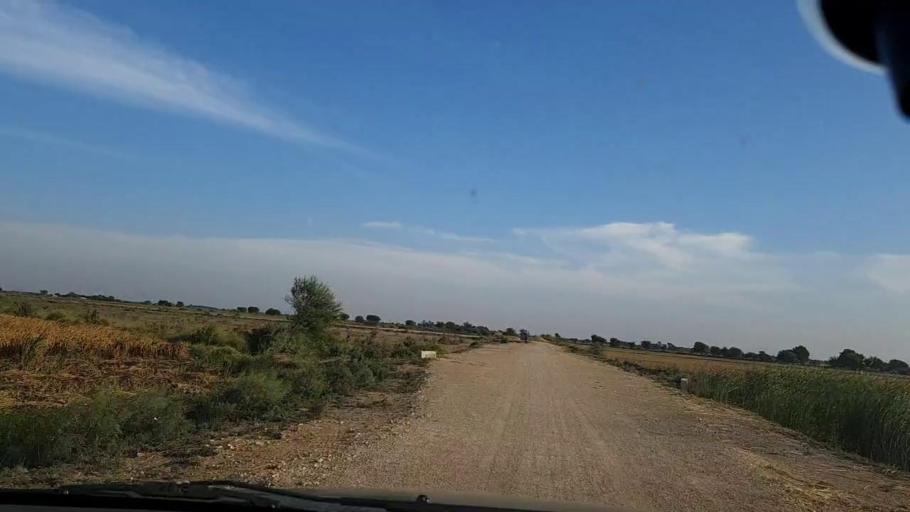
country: PK
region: Sindh
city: Mirpur Batoro
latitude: 24.6584
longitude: 68.3019
